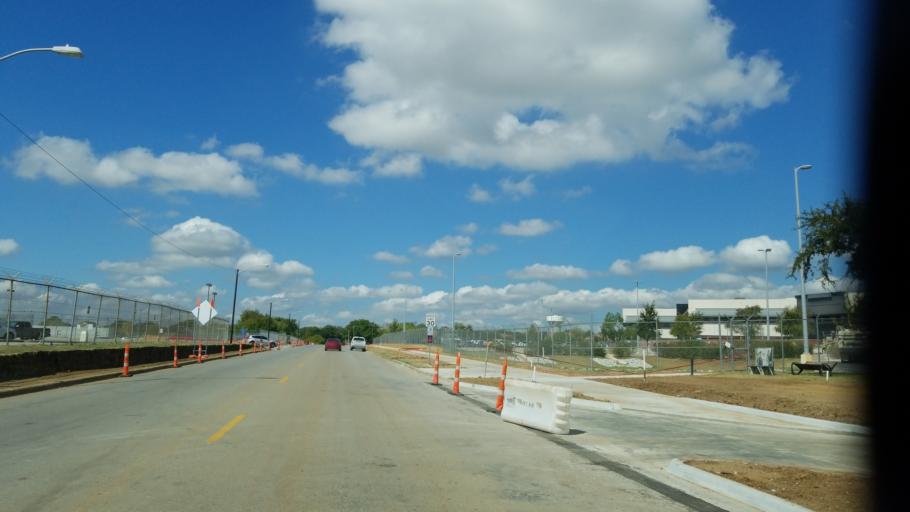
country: US
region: Texas
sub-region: Tarrant County
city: Euless
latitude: 32.8321
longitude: -97.0662
